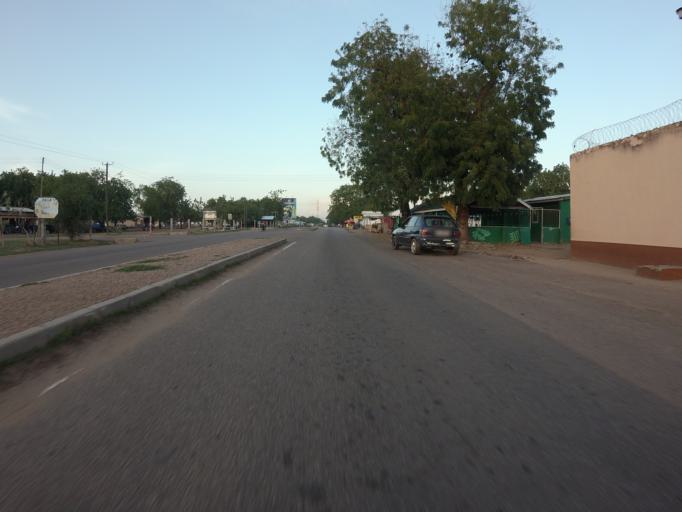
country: GH
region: Upper East
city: Navrongo
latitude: 10.8962
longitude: -1.0911
